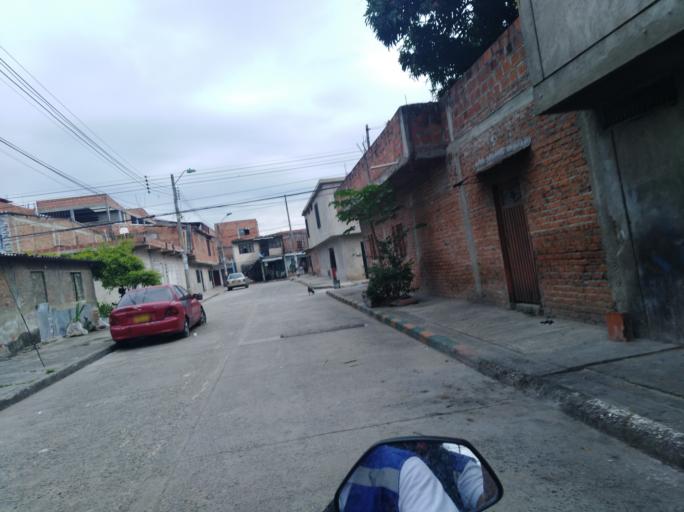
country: CO
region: Valle del Cauca
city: Cali
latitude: 3.4749
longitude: -76.4787
